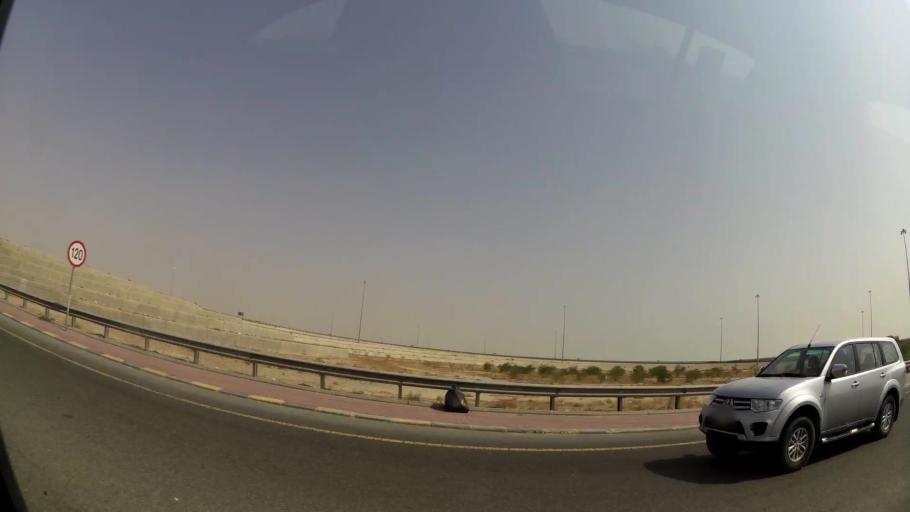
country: KW
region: Muhafazat al Jahra'
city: Al Jahra'
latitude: 29.3729
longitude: 47.6624
